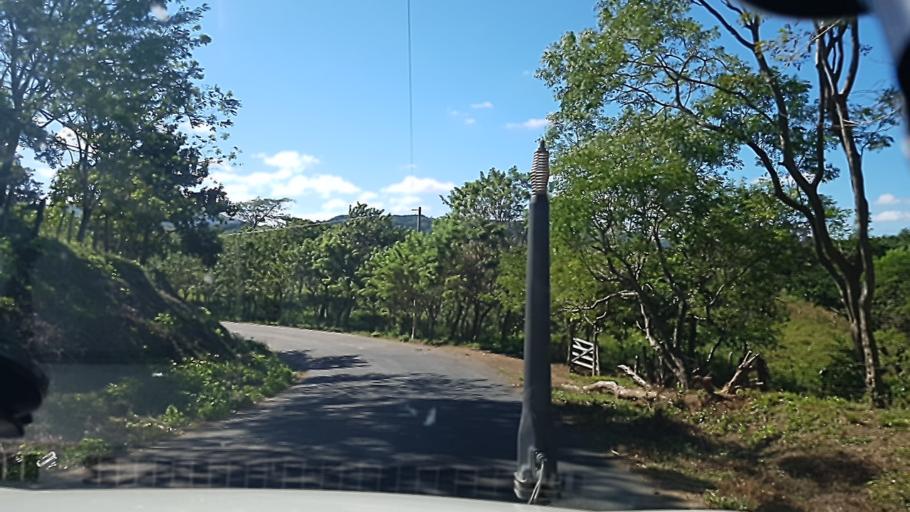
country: NI
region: Carazo
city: Santa Teresa
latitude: 11.7147
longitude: -86.1812
